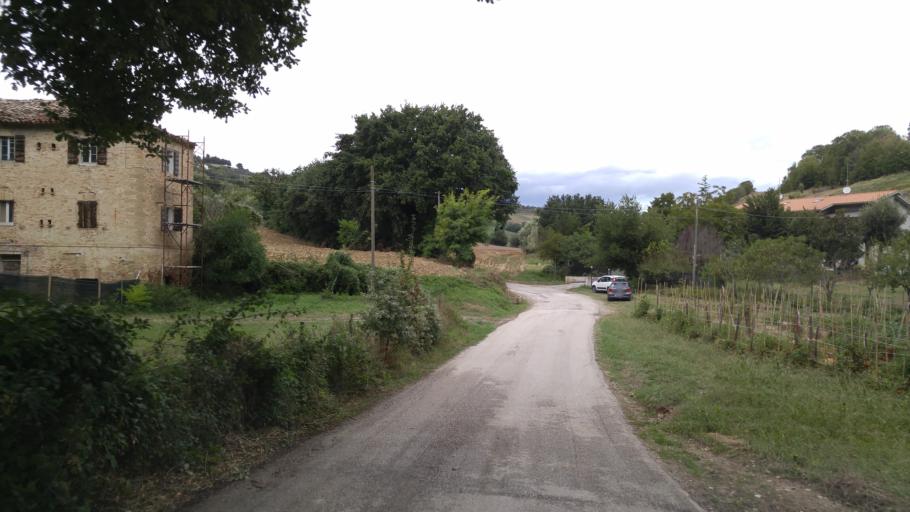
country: IT
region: The Marches
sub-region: Provincia di Pesaro e Urbino
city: Cartoceto
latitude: 43.7865
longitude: 12.8861
